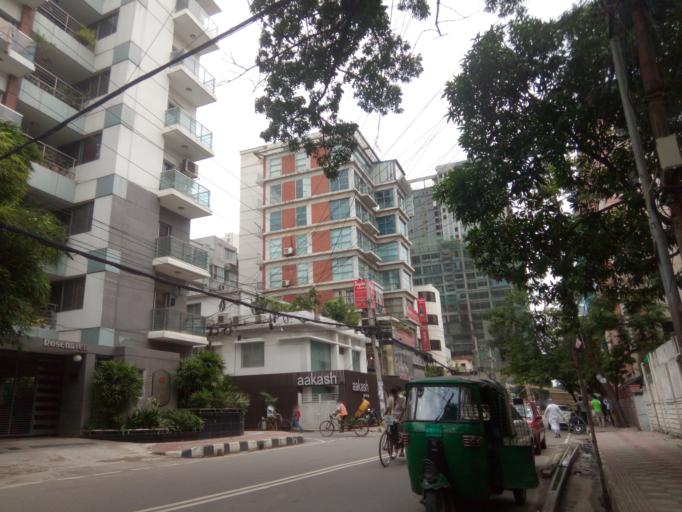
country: BD
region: Dhaka
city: Paltan
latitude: 23.7915
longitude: 90.4064
